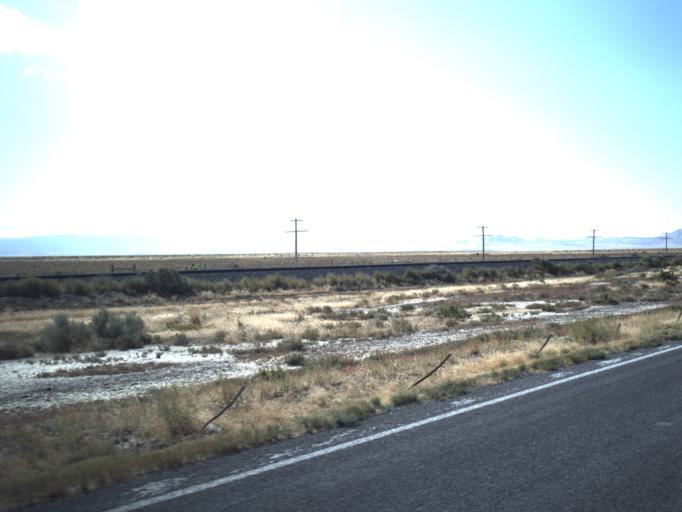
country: US
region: Utah
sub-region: Millard County
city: Delta
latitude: 38.9448
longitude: -112.8072
